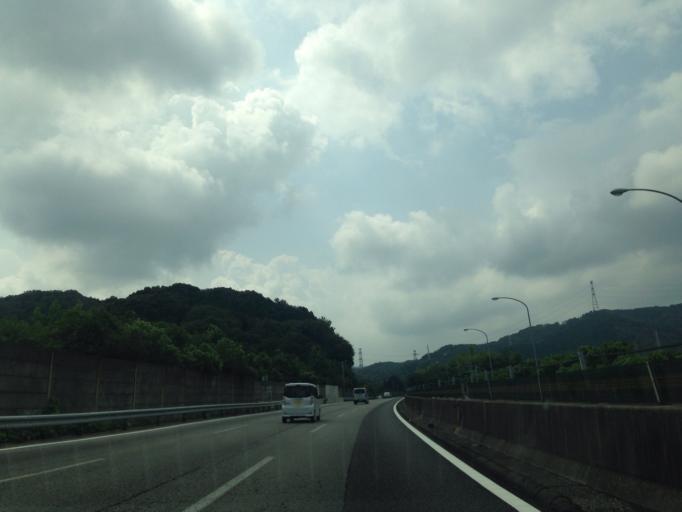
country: JP
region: Aichi
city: Gamagori
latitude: 34.8886
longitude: 137.2652
